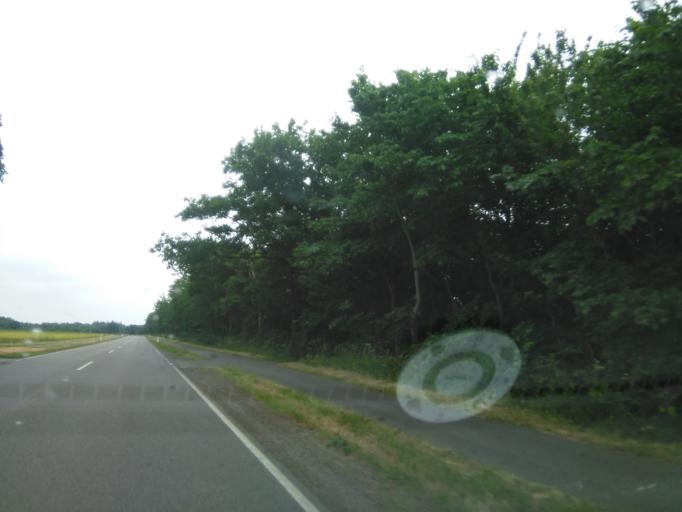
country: DK
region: Capital Region
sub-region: Bornholm Kommune
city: Ronne
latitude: 55.0537
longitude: 14.7997
